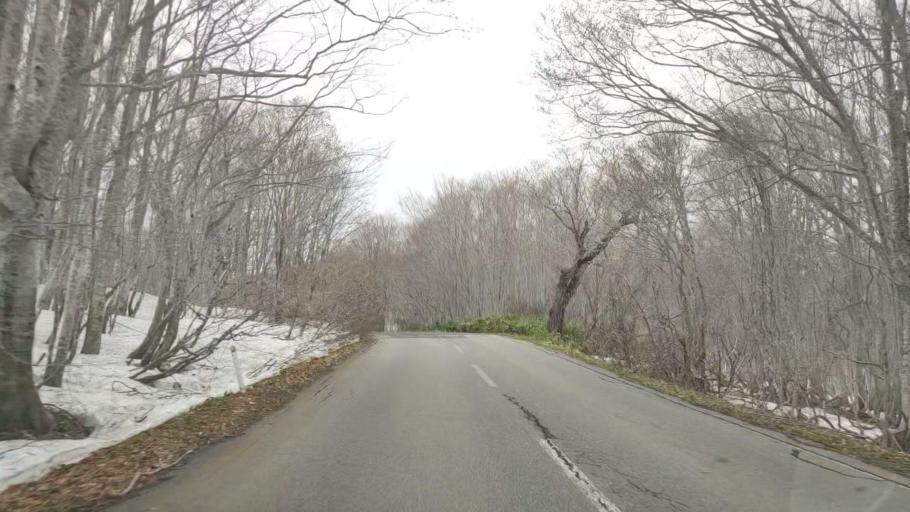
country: JP
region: Aomori
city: Aomori Shi
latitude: 40.6441
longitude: 140.9416
